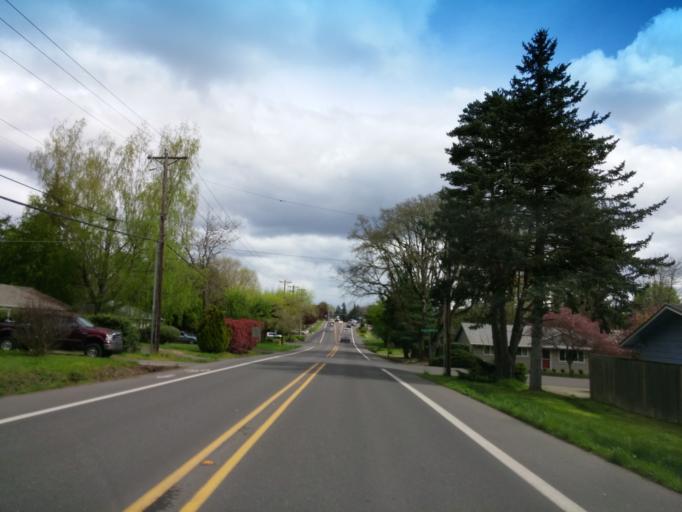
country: US
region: Oregon
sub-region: Washington County
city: Cedar Hills
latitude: 45.5030
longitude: -122.8105
